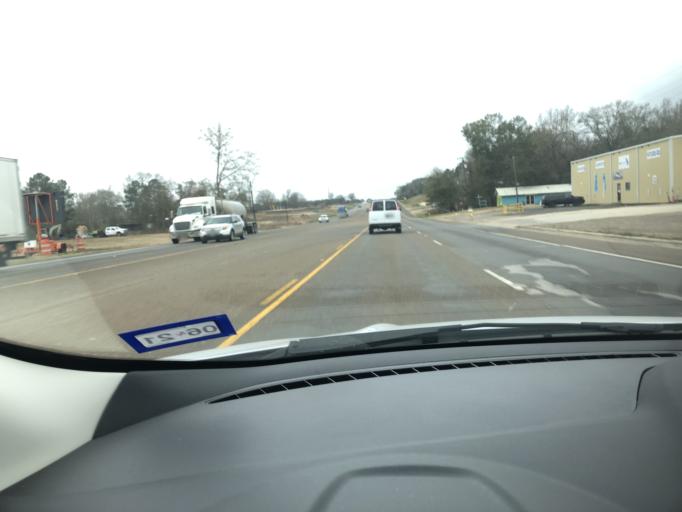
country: US
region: Texas
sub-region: Nacogdoches County
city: Nacogdoches
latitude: 31.5604
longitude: -94.6811
